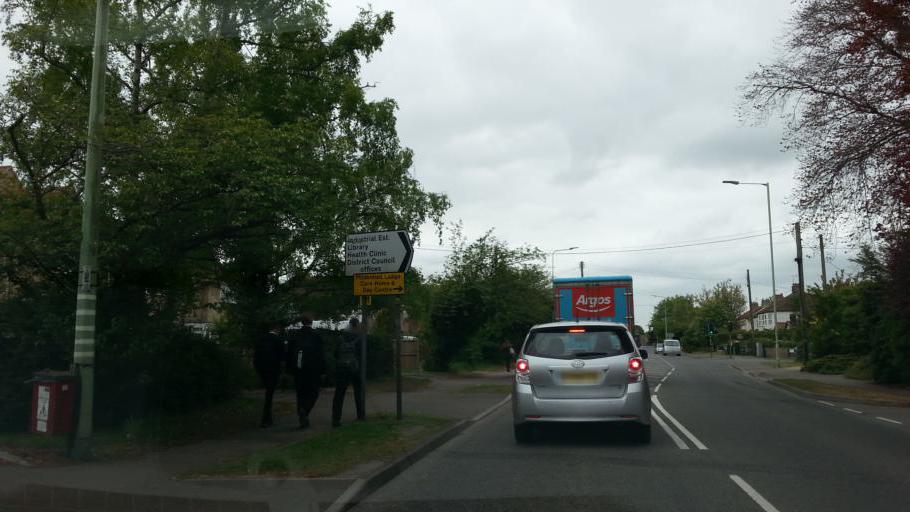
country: GB
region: England
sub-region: Suffolk
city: Lakenheath
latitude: 52.3444
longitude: 0.5193
